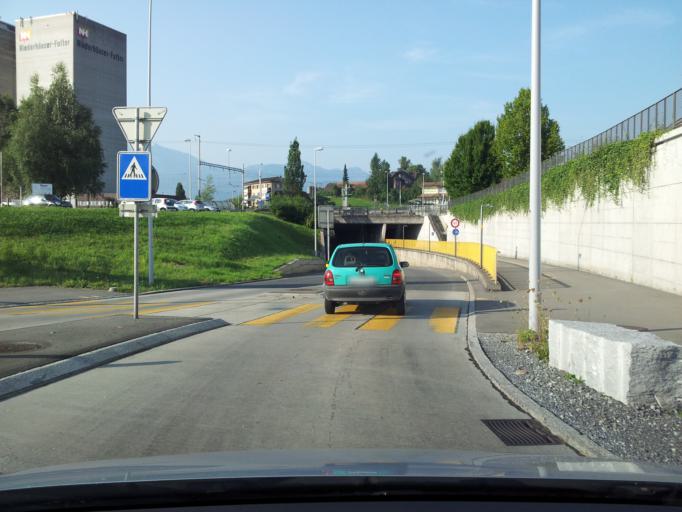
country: CH
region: Lucerne
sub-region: Hochdorf District
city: Emmen
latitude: 47.0891
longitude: 8.2500
